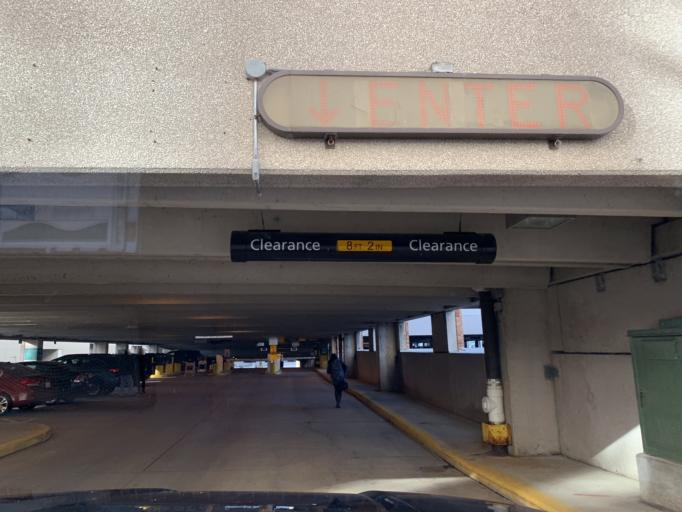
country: US
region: Wisconsin
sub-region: Outagamie County
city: Appleton
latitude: 44.2624
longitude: -88.4088
